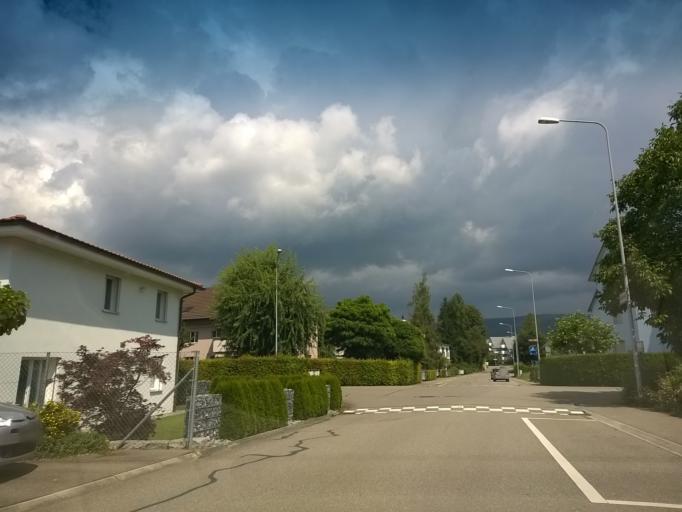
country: CH
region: Zurich
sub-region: Bezirk Buelach
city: Embrach
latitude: 47.5076
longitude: 8.5958
